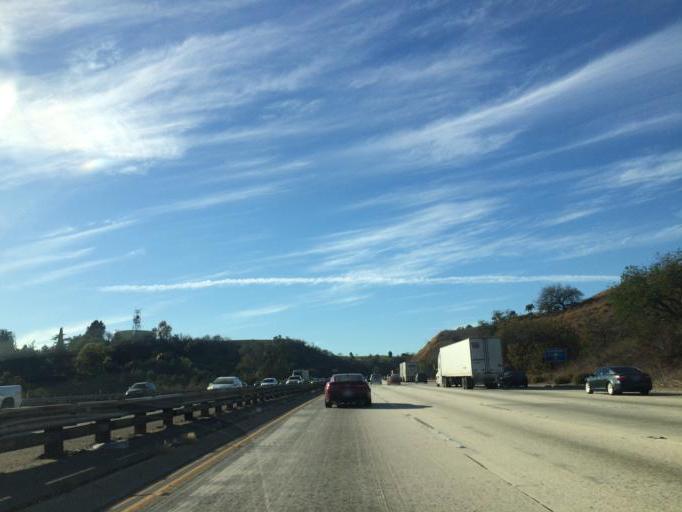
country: US
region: California
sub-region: Los Angeles County
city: Diamond Bar
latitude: 34.0638
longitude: -117.8208
